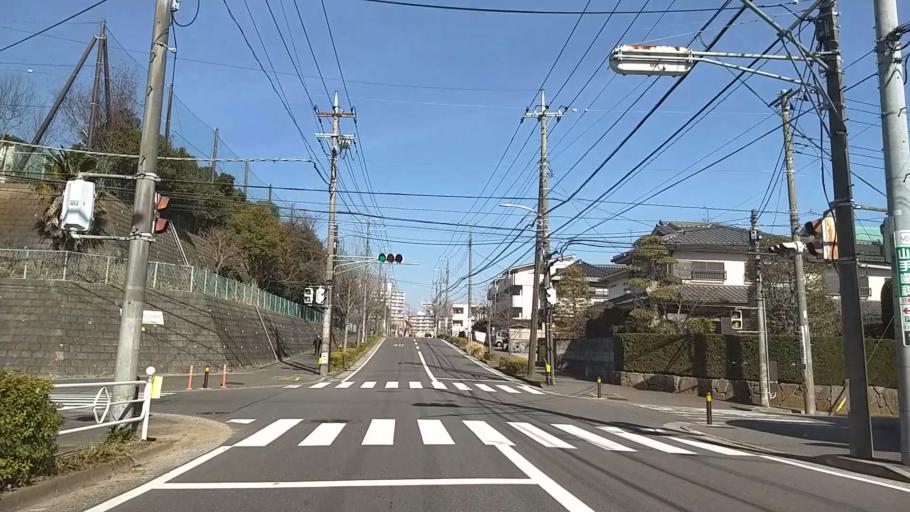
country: JP
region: Kanagawa
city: Kamakura
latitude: 35.3701
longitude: 139.5886
